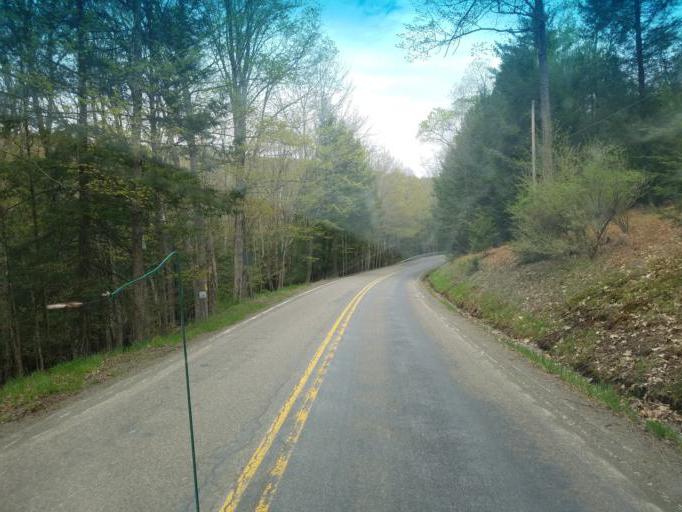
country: US
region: Pennsylvania
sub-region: Tioga County
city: Wellsboro
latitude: 41.7008
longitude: -77.4442
